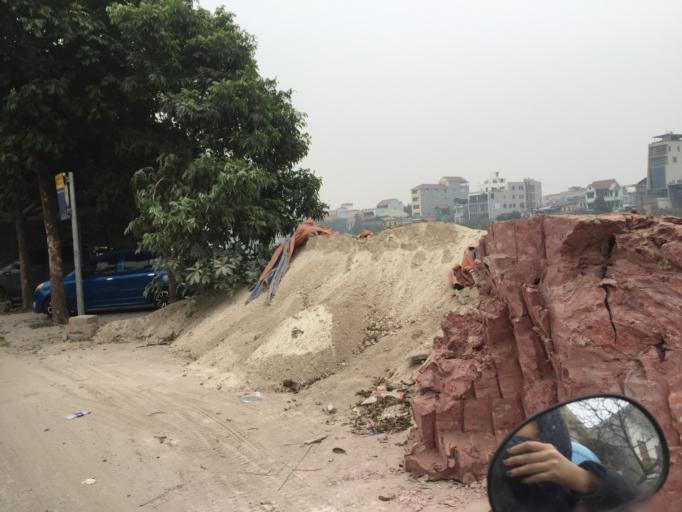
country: VN
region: Hung Yen
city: Van Giang
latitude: 20.9714
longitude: 105.9165
